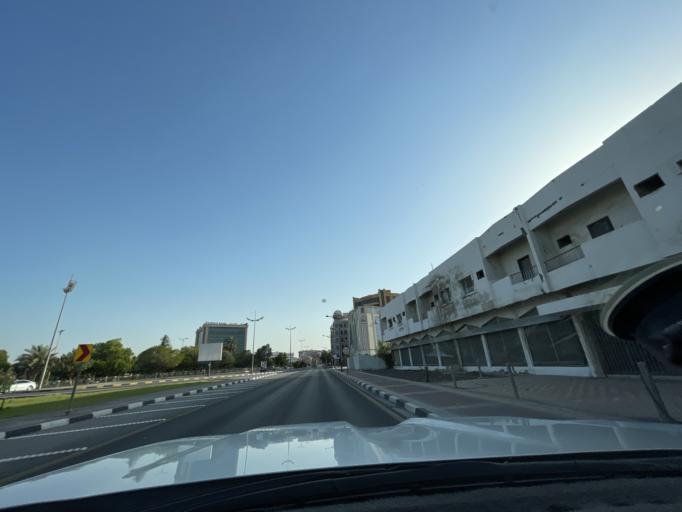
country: SA
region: Eastern Province
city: Khobar
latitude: 26.2850
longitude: 50.2055
